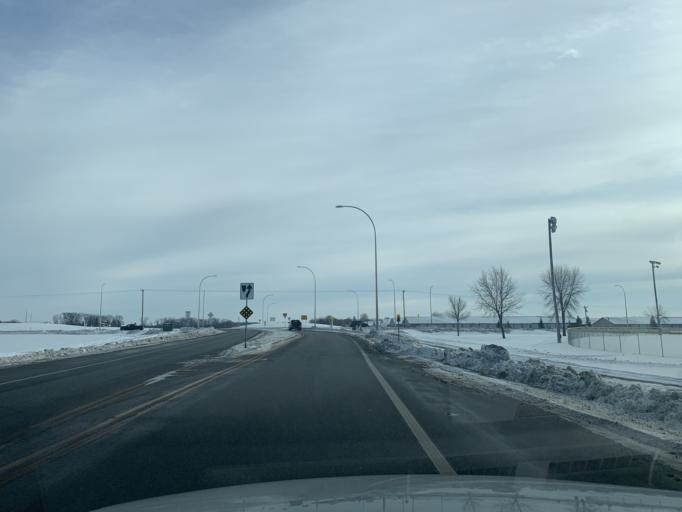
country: US
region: Minnesota
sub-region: Wright County
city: Buffalo
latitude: 45.1655
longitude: -93.8494
